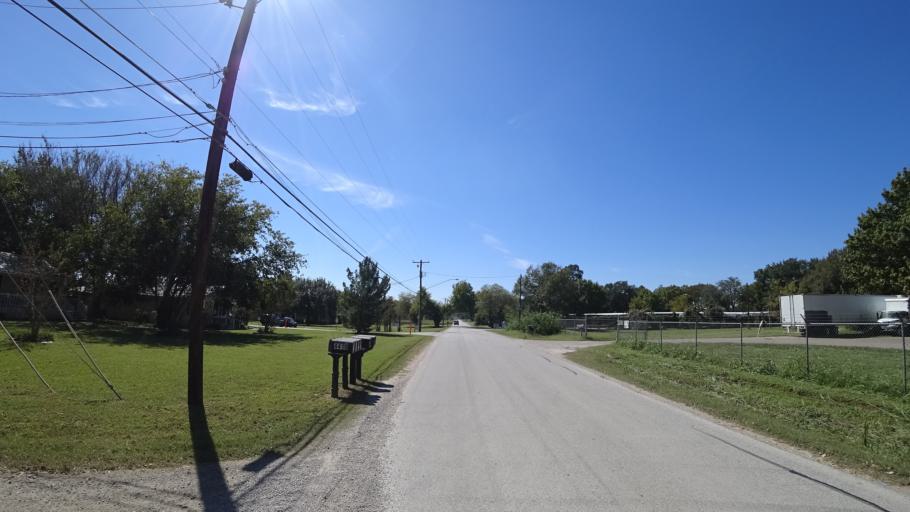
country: US
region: Texas
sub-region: Travis County
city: Hornsby Bend
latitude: 30.2733
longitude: -97.6496
